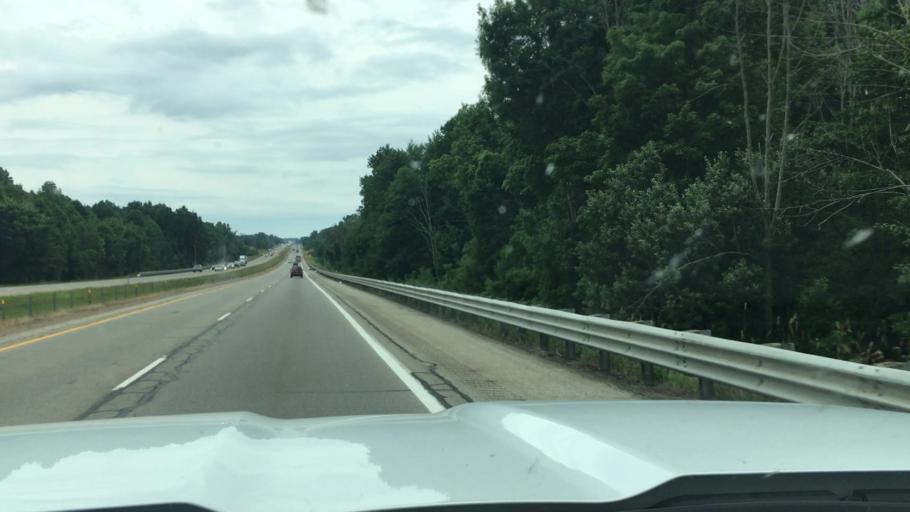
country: US
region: Michigan
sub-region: Allegan County
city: Wayland
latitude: 42.5736
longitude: -85.6627
